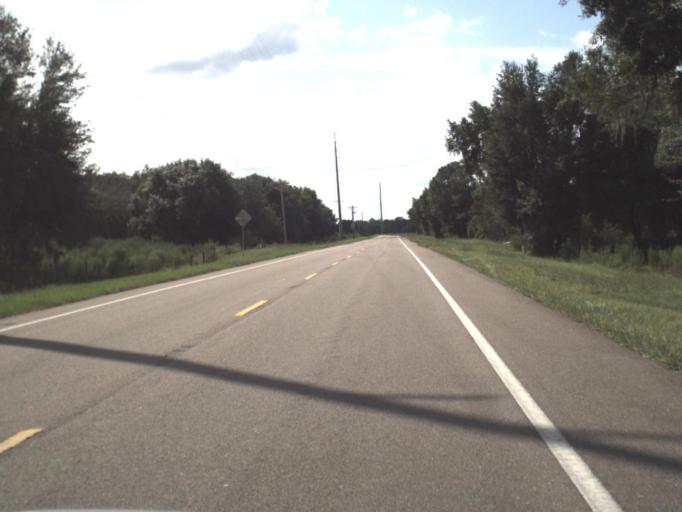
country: US
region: Florida
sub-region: Hardee County
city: Zolfo Springs
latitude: 27.4829
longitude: -81.9311
